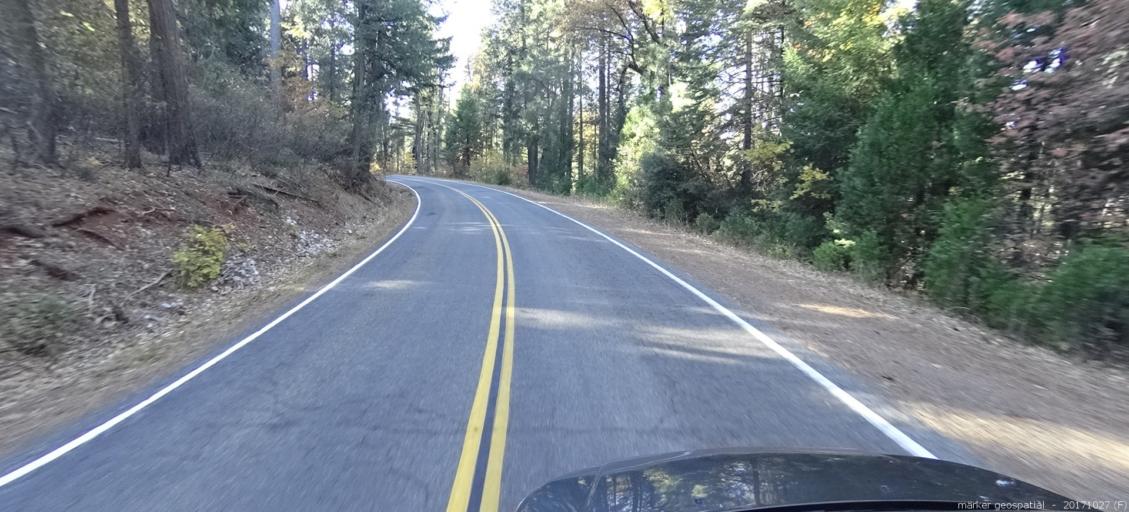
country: US
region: California
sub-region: Shasta County
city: Burney
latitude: 40.8896
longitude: -121.9075
